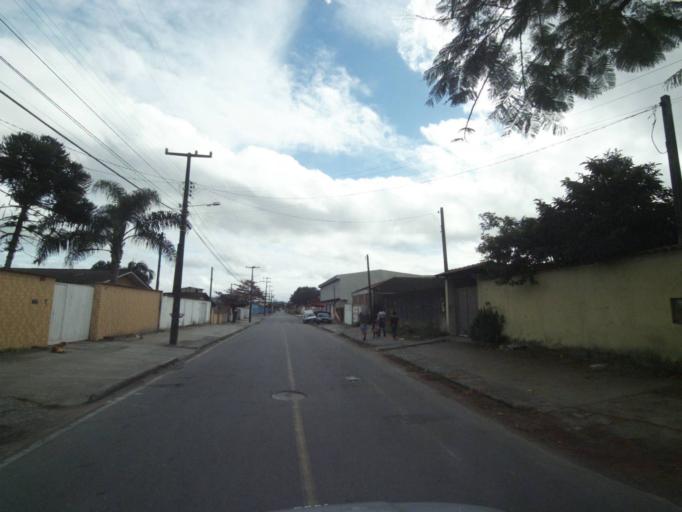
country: BR
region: Parana
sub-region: Paranagua
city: Paranagua
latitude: -25.5686
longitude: -48.5641
